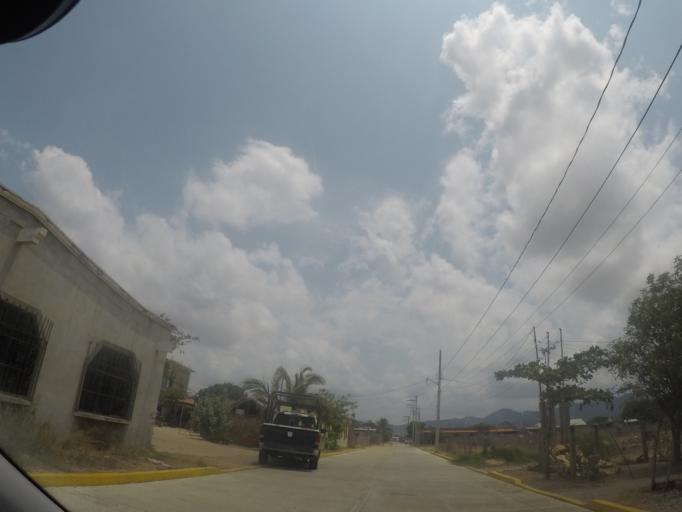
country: MX
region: Oaxaca
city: El Espinal
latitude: 16.5557
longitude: -94.9444
